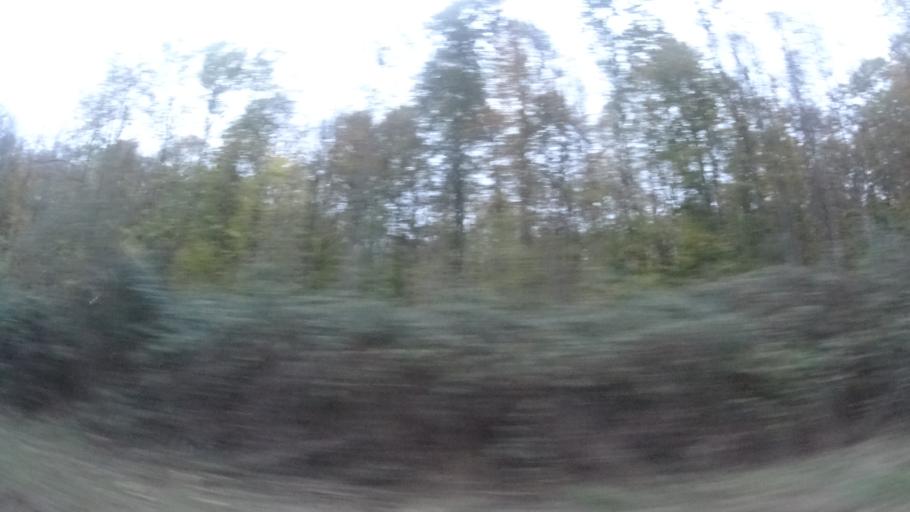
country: DE
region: Hesse
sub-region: Regierungsbezirk Darmstadt
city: Steinau an der Strasse
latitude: 50.3395
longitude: 9.4266
